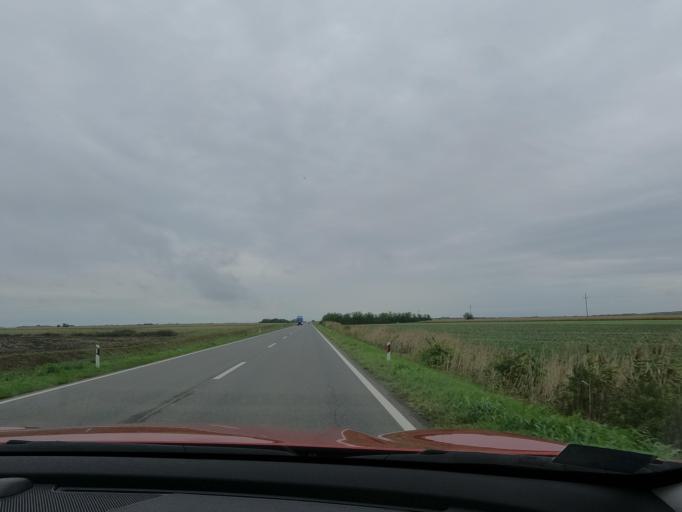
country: RS
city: Banatska Topola
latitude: 45.6973
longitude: 20.4211
